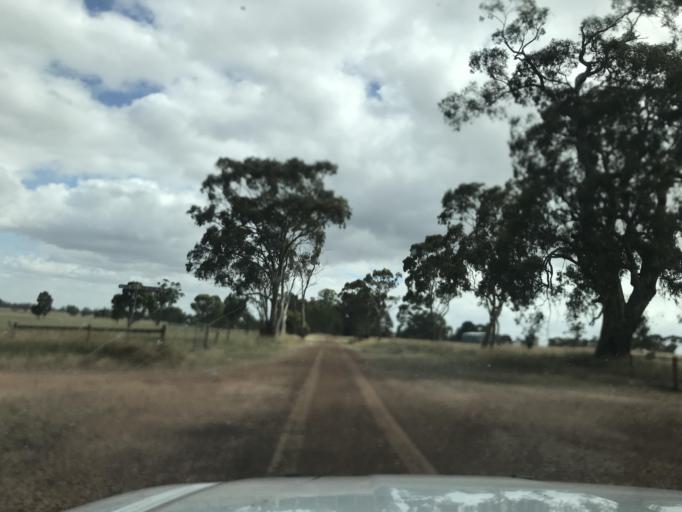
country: AU
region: South Australia
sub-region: Naracoorte and Lucindale
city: Naracoorte
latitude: -36.9003
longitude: 141.4016
